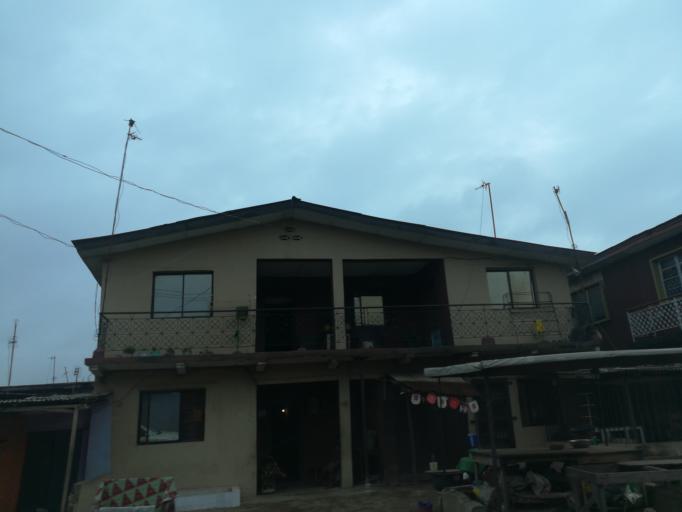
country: NG
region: Lagos
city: Oshodi
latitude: 6.5640
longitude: 3.3421
